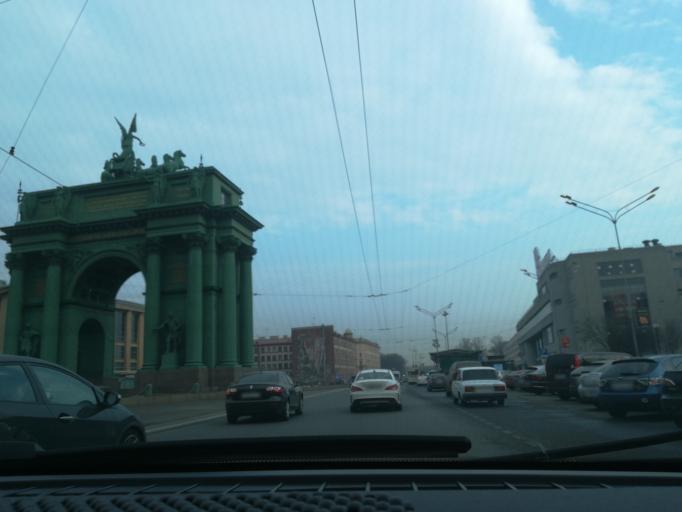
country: RU
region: St.-Petersburg
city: Admiralteisky
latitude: 59.9012
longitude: 30.2729
